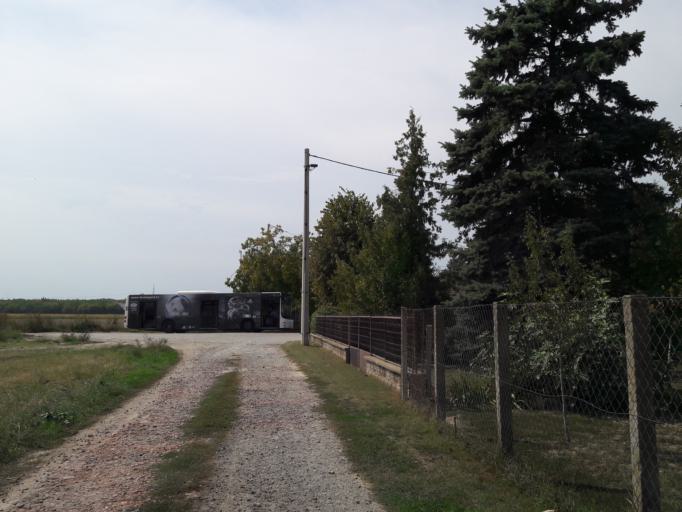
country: HR
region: Osjecko-Baranjska
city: Brijest
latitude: 45.5171
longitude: 18.6295
